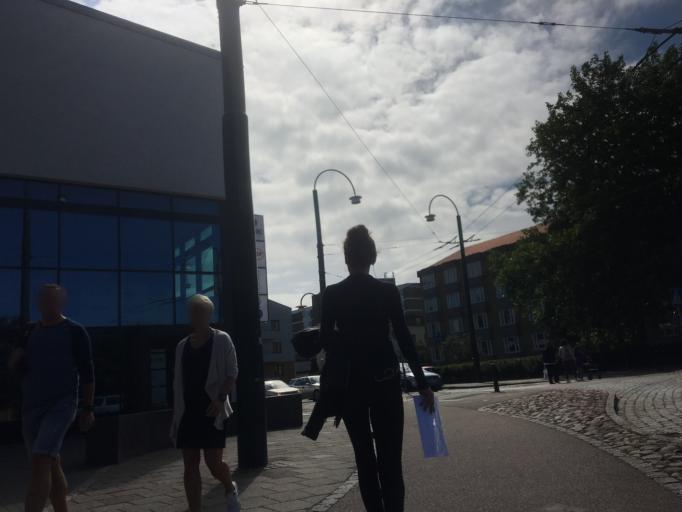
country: SE
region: Skane
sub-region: Landskrona
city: Landskrona
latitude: 55.8757
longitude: 12.8326
